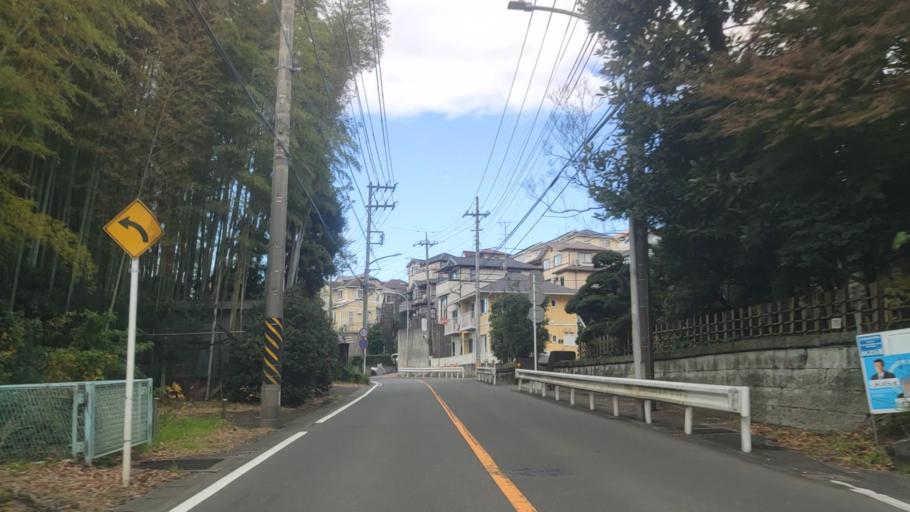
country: JP
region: Kanagawa
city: Minami-rinkan
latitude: 35.4280
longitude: 139.5191
